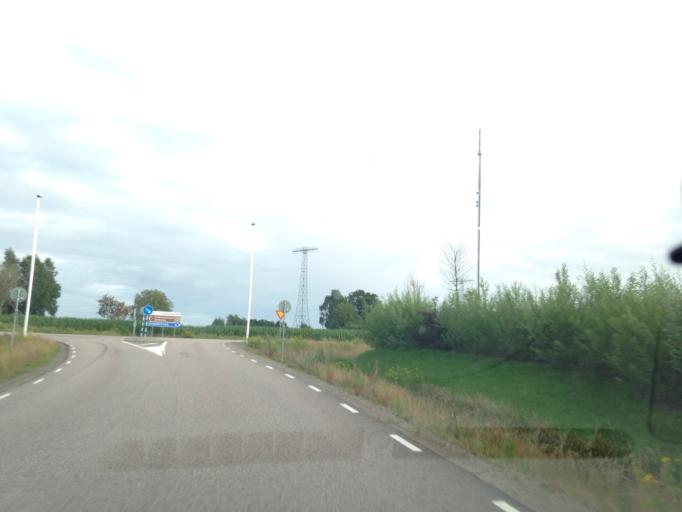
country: SE
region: Halland
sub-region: Varbergs Kommun
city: Tvaaker
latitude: 57.1151
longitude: 12.3928
